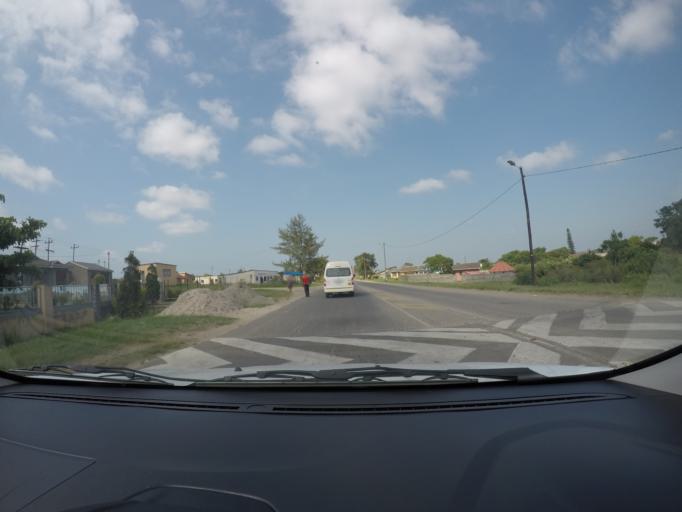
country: ZA
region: KwaZulu-Natal
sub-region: uThungulu District Municipality
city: eSikhawini
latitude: -28.8861
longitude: 31.8993
